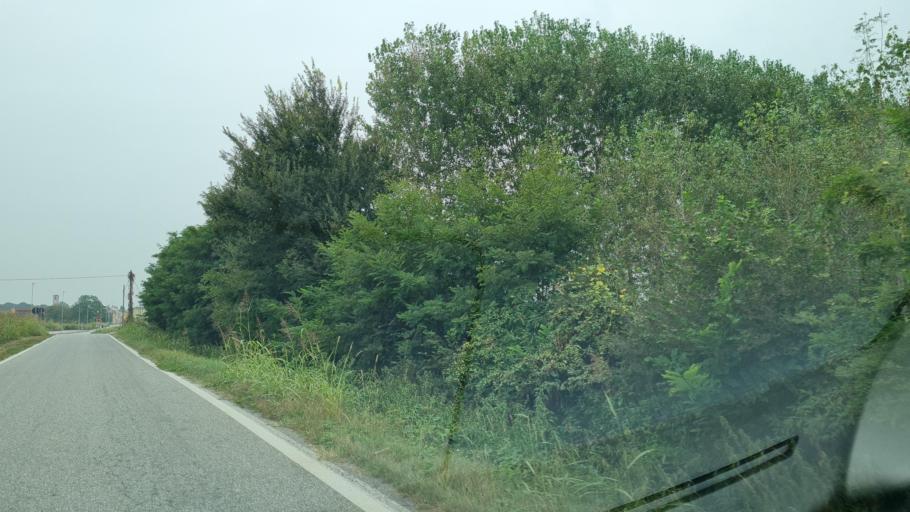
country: IT
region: Piedmont
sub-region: Provincia di Novara
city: Landiona
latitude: 45.4960
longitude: 8.4311
